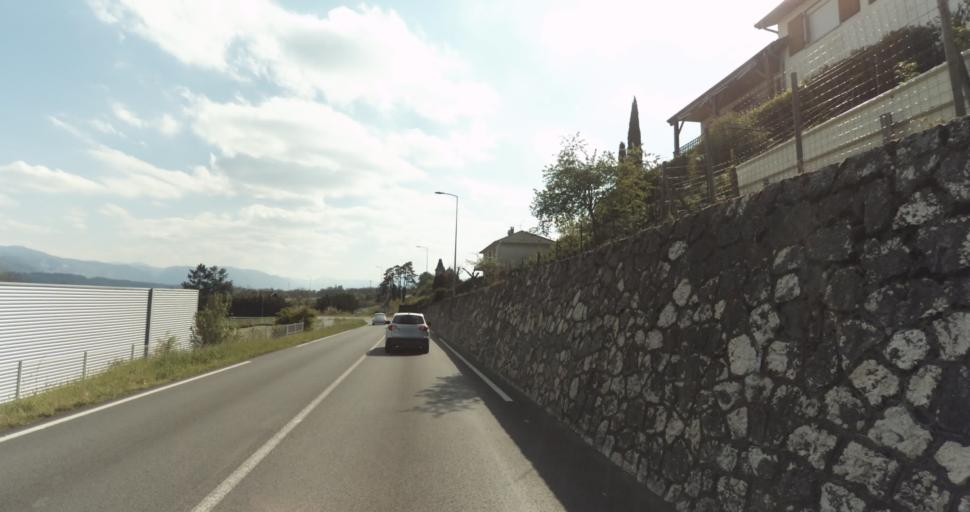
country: FR
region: Rhone-Alpes
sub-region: Departement de l'Isere
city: Saint-Marcellin
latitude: 45.1417
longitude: 5.3258
